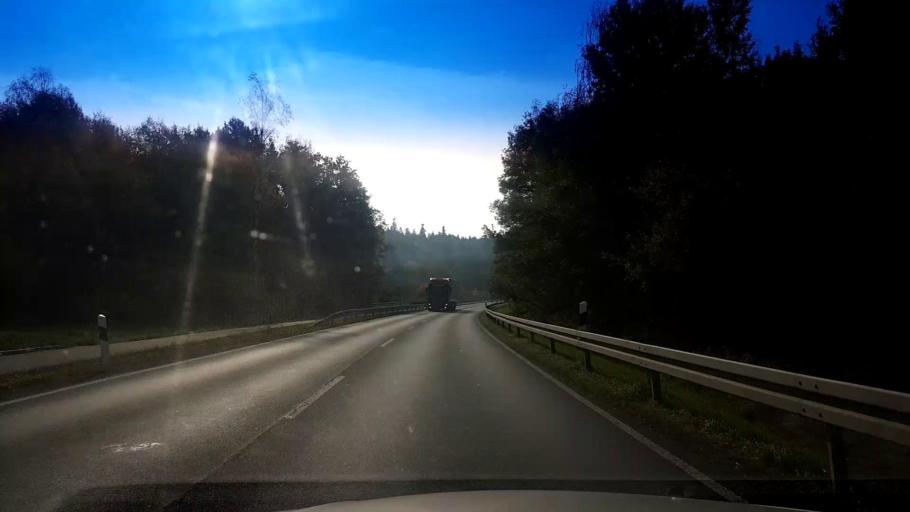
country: DE
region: Bavaria
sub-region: Upper Franconia
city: Neuenmarkt
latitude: 50.0906
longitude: 11.6094
